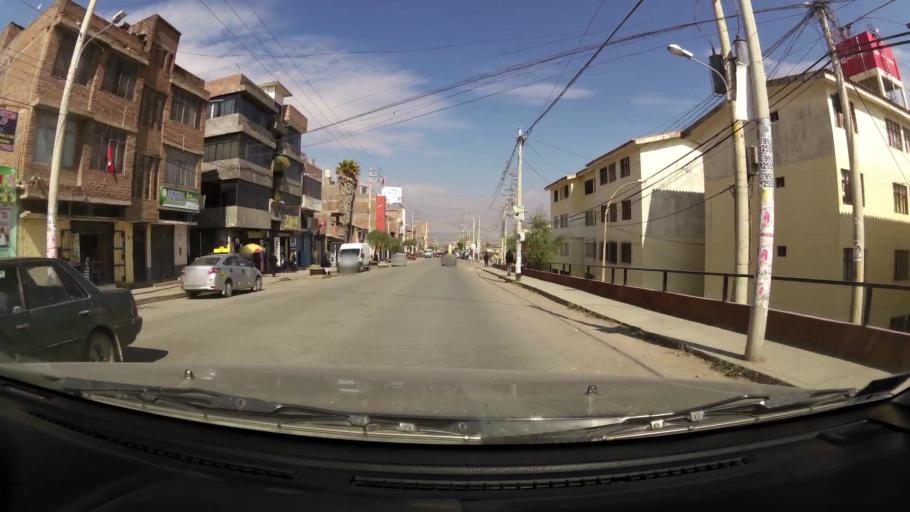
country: PE
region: Junin
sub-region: Provincia de Huancayo
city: El Tambo
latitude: -12.0726
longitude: -75.2200
